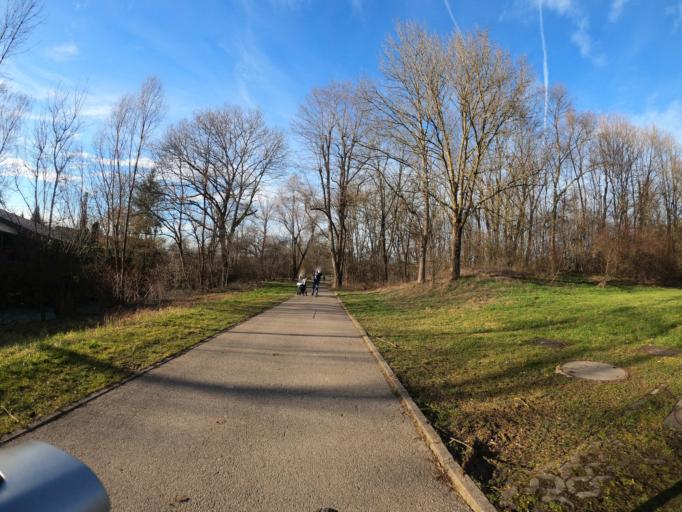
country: DE
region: Baden-Wuerttemberg
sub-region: Regierungsbezirk Stuttgart
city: Wernau
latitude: 48.6621
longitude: 9.4124
